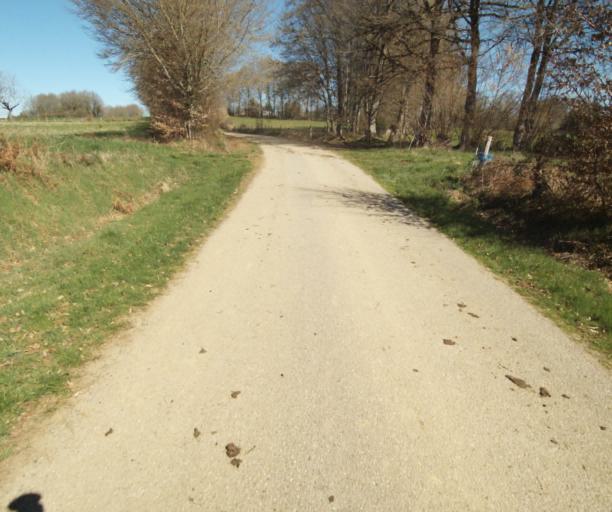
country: FR
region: Limousin
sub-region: Departement de la Correze
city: Chamboulive
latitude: 45.4214
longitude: 1.7217
